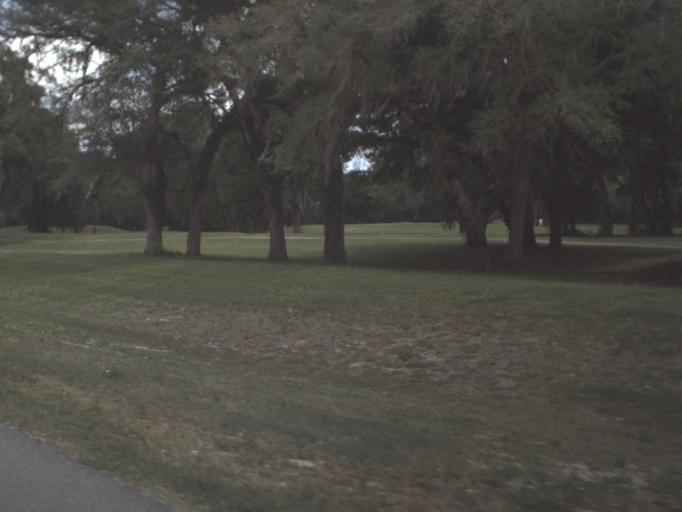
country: US
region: Florida
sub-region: Citrus County
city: Hernando
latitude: 29.0287
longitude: -82.3088
